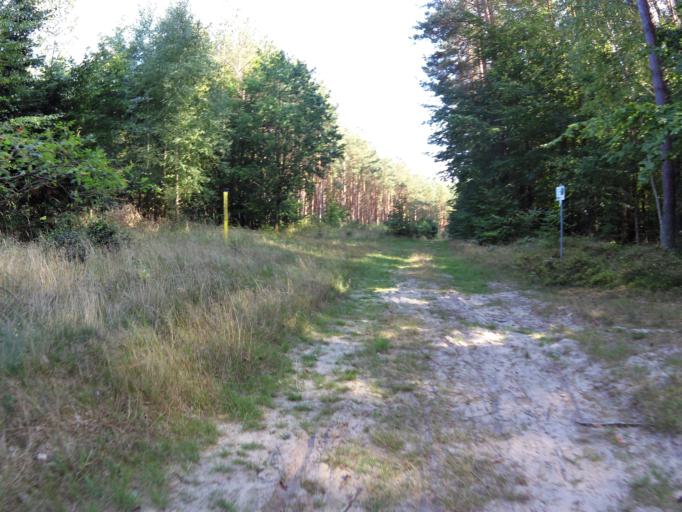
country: DE
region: Mecklenburg-Vorpommern
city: Loddin
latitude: 54.0053
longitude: 14.0562
